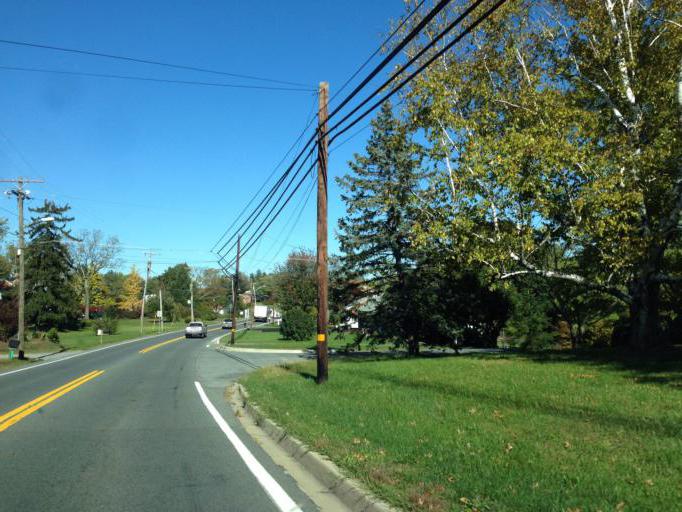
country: US
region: Maryland
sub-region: Montgomery County
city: Damascus
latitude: 39.2973
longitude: -77.2036
